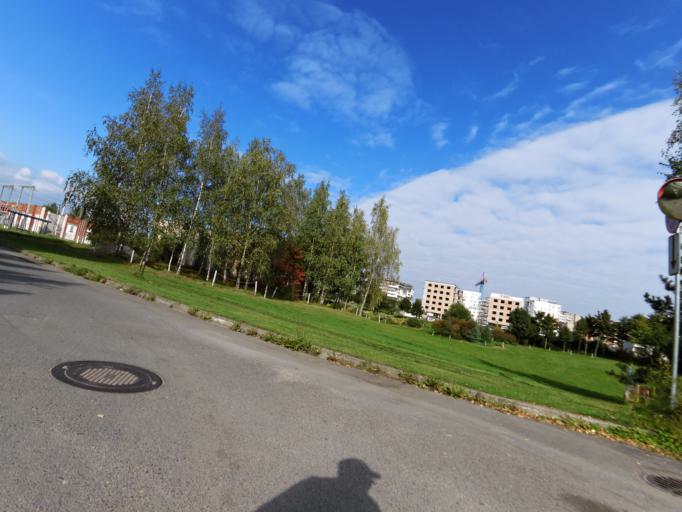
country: LT
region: Vilnius County
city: Pilaite
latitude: 54.7012
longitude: 25.1730
